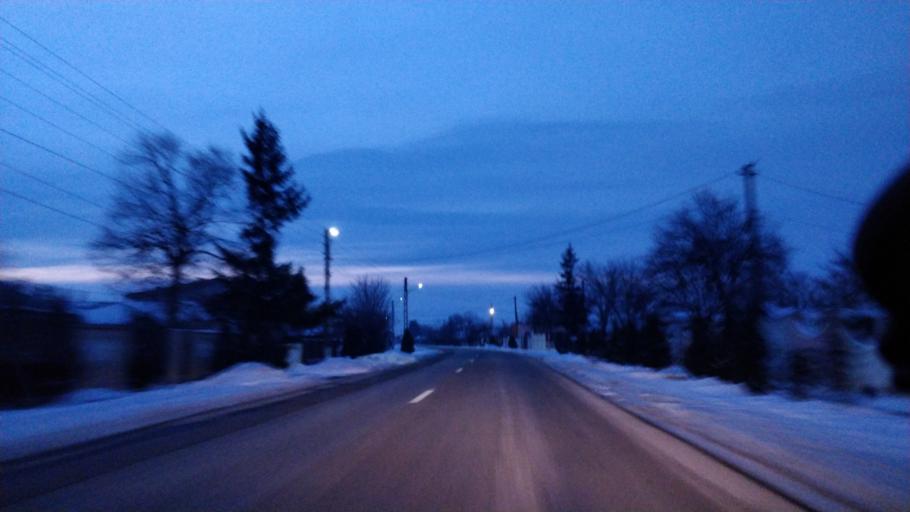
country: RO
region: Vrancea
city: Vulturu de Sus
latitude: 45.6133
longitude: 27.4357
